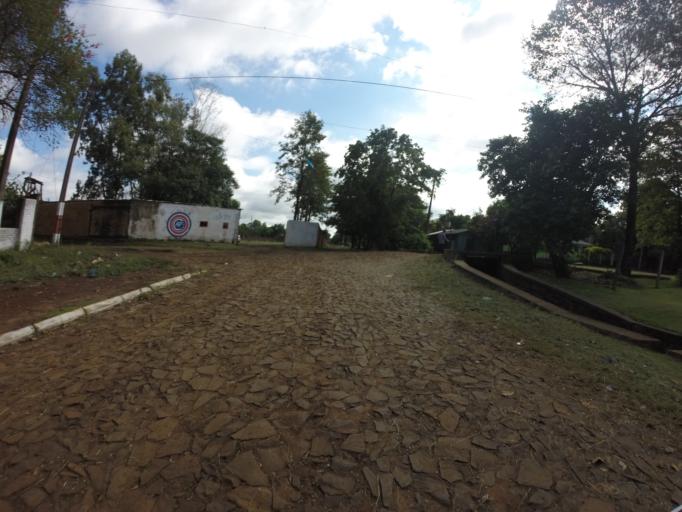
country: PY
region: Alto Parana
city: Ciudad del Este
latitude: -25.3981
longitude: -54.6499
